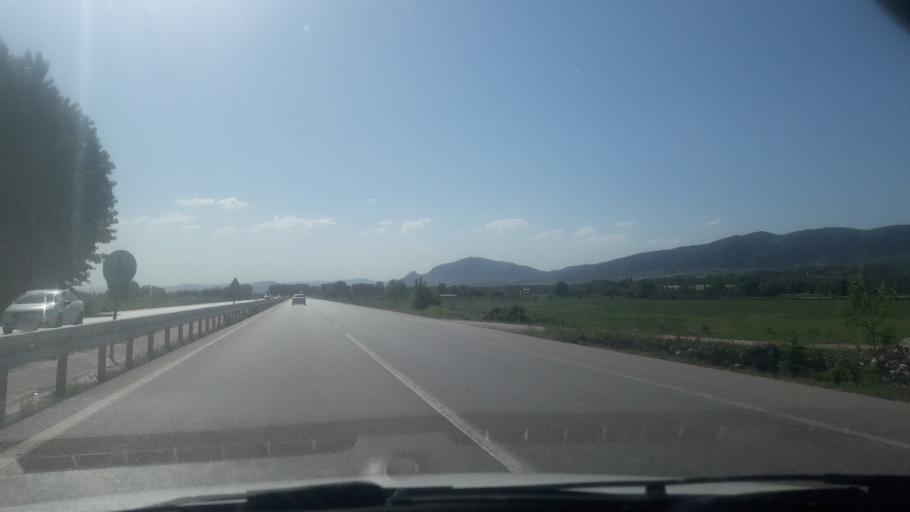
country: TR
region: Tokat
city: Dokmetepe
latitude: 40.3040
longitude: 36.3175
